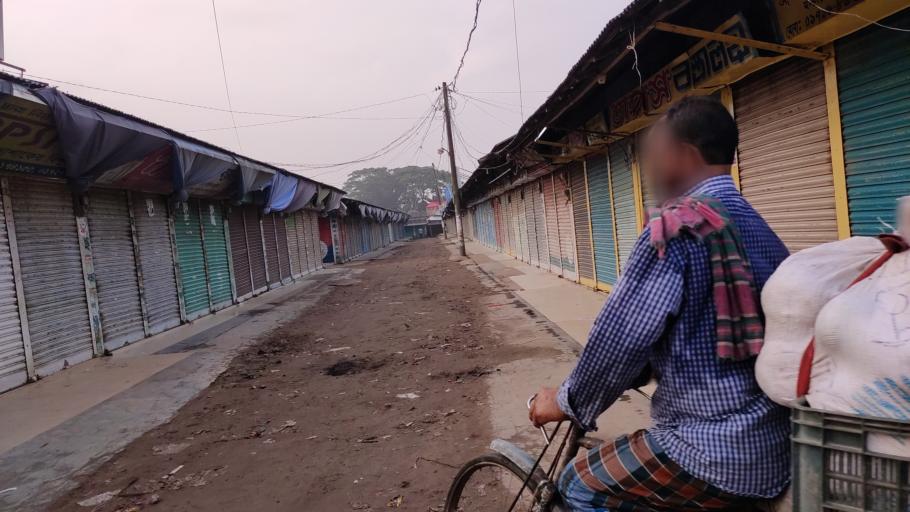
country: BD
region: Dhaka
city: Netrakona
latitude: 24.7167
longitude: 90.9481
